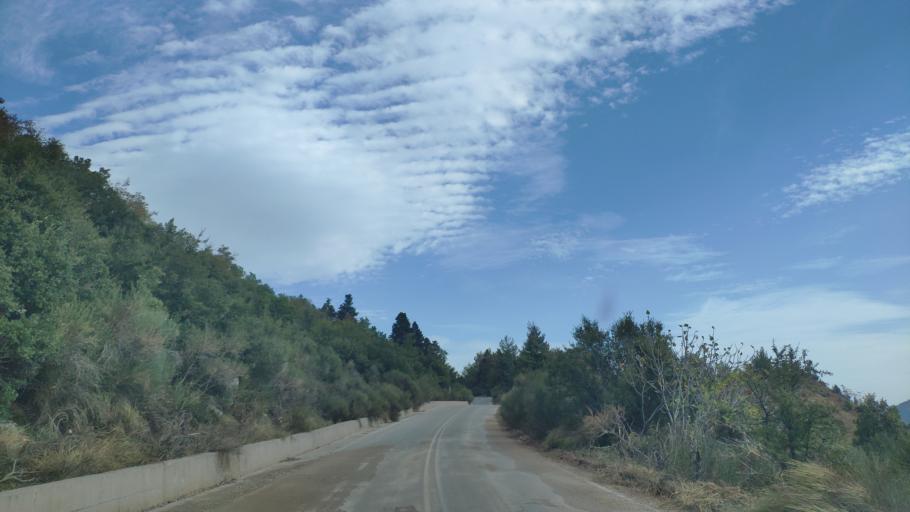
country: GR
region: Central Greece
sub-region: Nomos Fokidos
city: Amfissa
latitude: 38.6416
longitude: 22.3846
